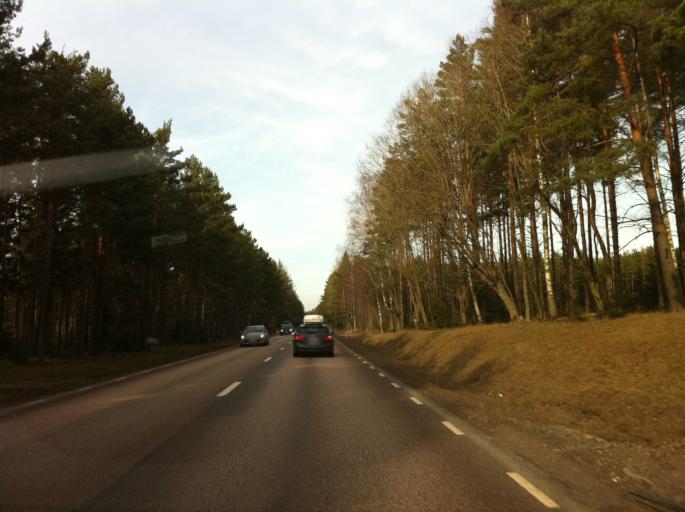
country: SE
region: Vaestra Goetaland
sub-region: Gullspangs Kommun
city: Gullspang
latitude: 59.0672
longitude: 14.1533
